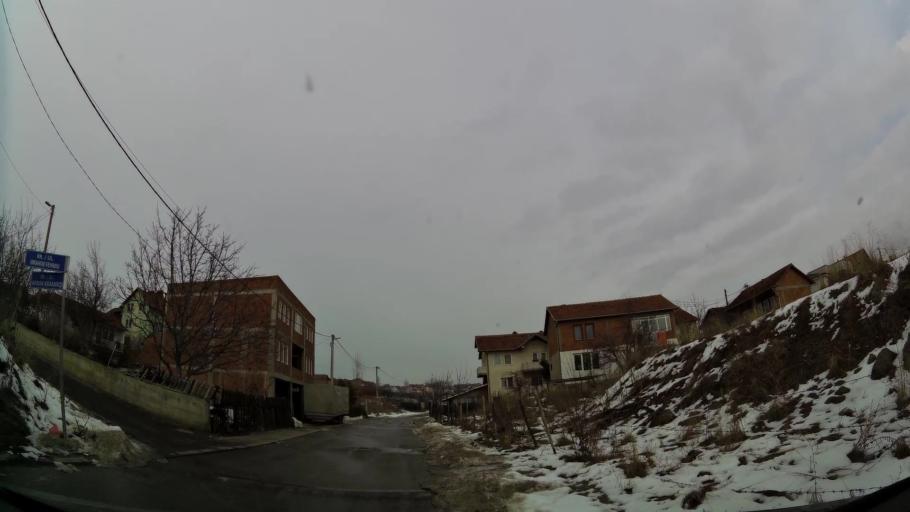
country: XK
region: Pristina
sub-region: Komuna e Prishtines
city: Pristina
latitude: 42.6849
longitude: 21.1625
